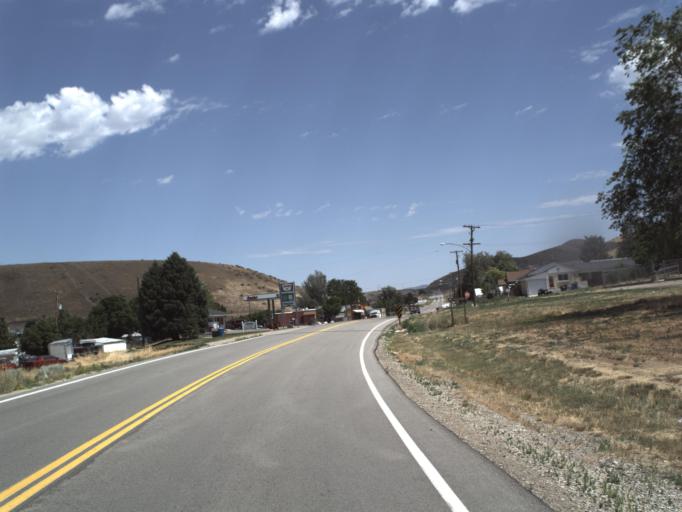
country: US
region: Utah
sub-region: Tooele County
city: Tooele
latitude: 40.4479
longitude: -112.3636
